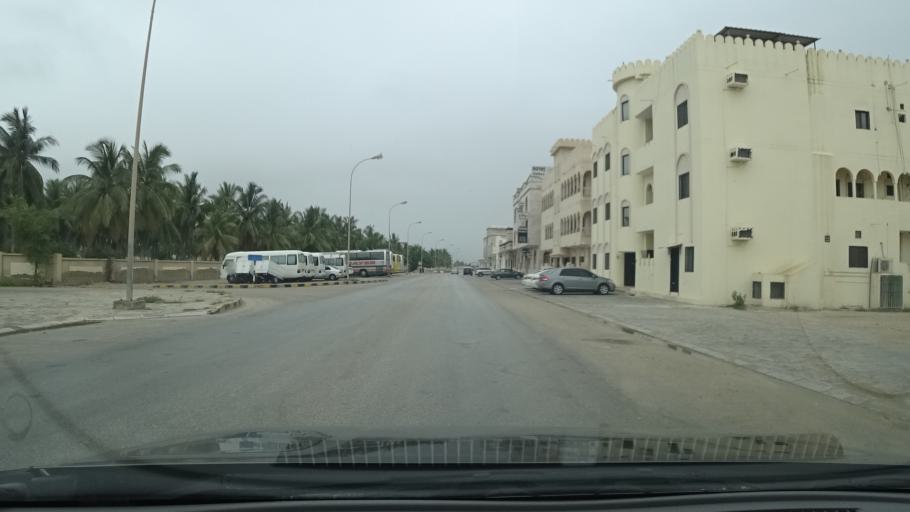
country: OM
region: Zufar
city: Salalah
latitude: 17.0227
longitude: 54.1631
